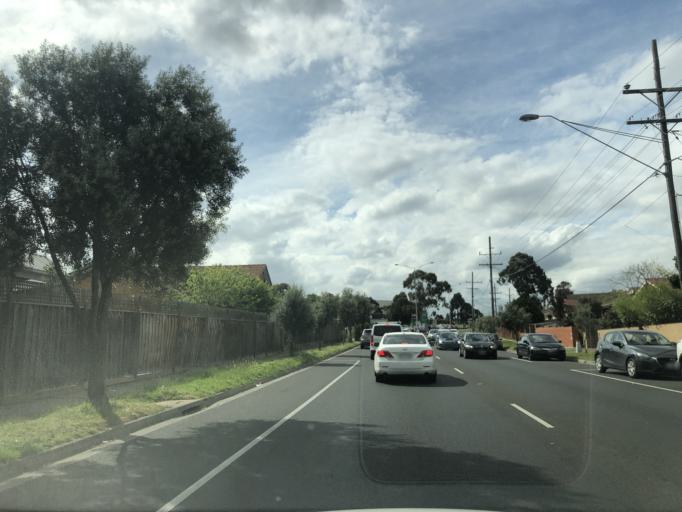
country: AU
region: Victoria
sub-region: Greater Dandenong
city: Noble Park North
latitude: -37.9397
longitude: 145.1925
